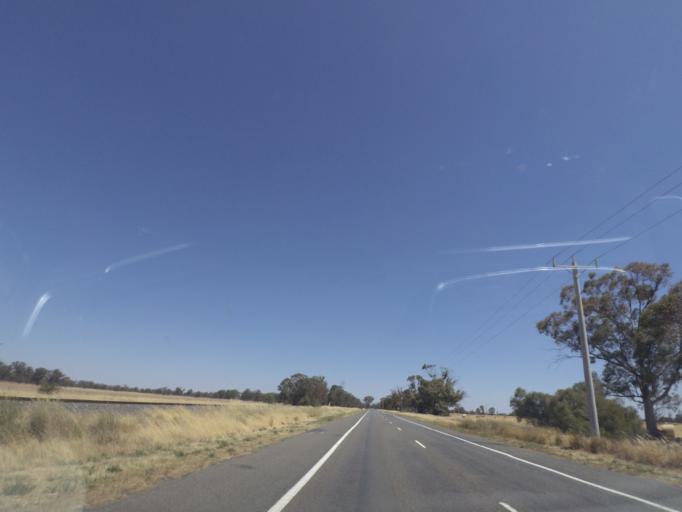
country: AU
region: Victoria
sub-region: Greater Shepparton
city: Shepparton
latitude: -36.2211
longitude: 145.4318
